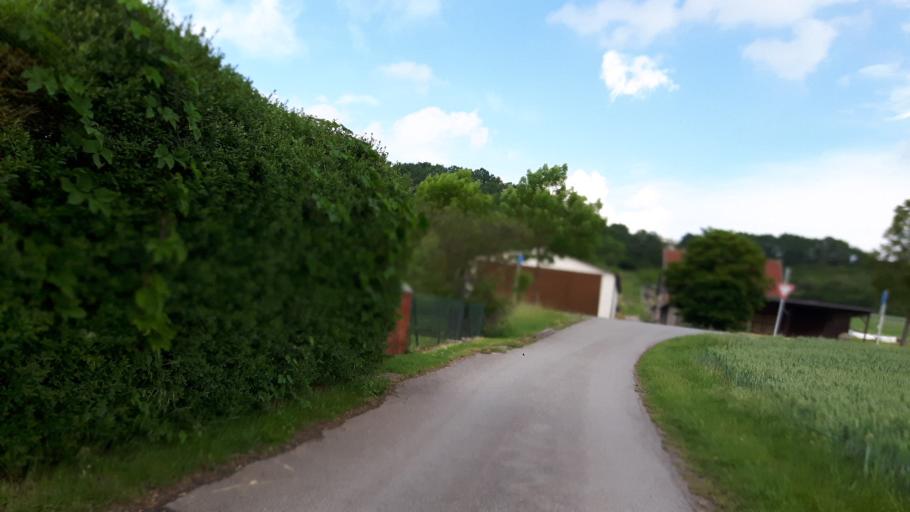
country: DE
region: Bavaria
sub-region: Regierungsbezirk Unterfranken
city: Herbstadt
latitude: 50.3113
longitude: 10.5318
